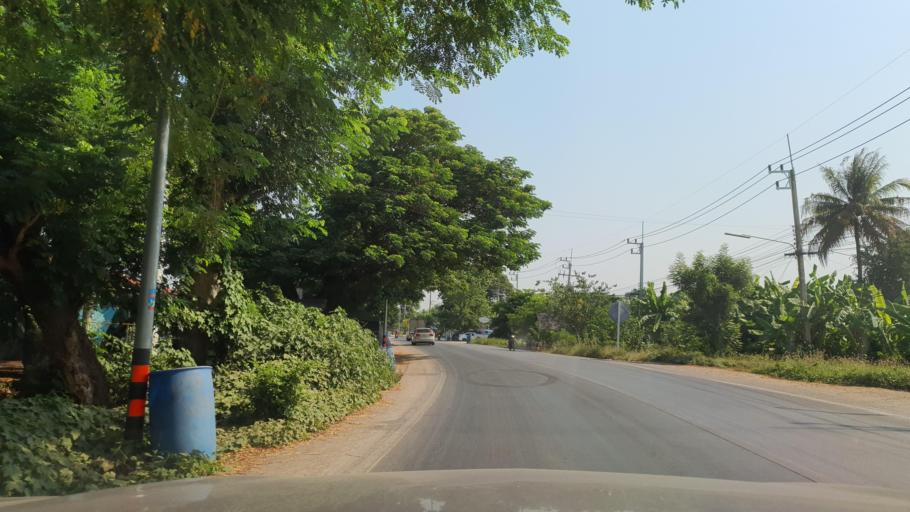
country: TH
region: Kanchanaburi
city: Kanchanaburi
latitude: 14.0526
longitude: 99.4738
